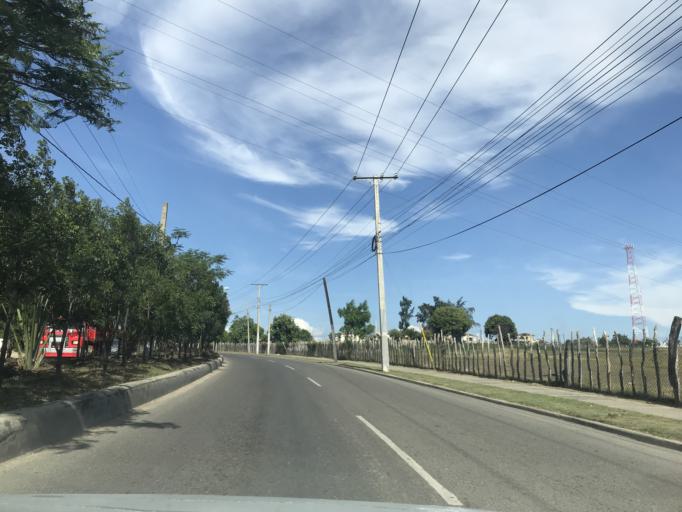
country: DO
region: Santiago
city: Santiago de los Caballeros
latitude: 19.4410
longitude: -70.7331
